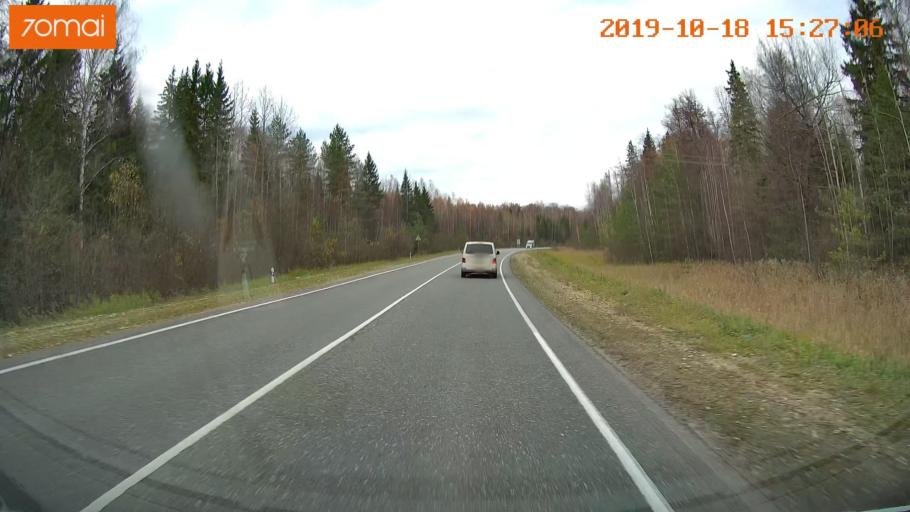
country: RU
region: Vladimir
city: Anopino
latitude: 55.7492
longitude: 40.6731
